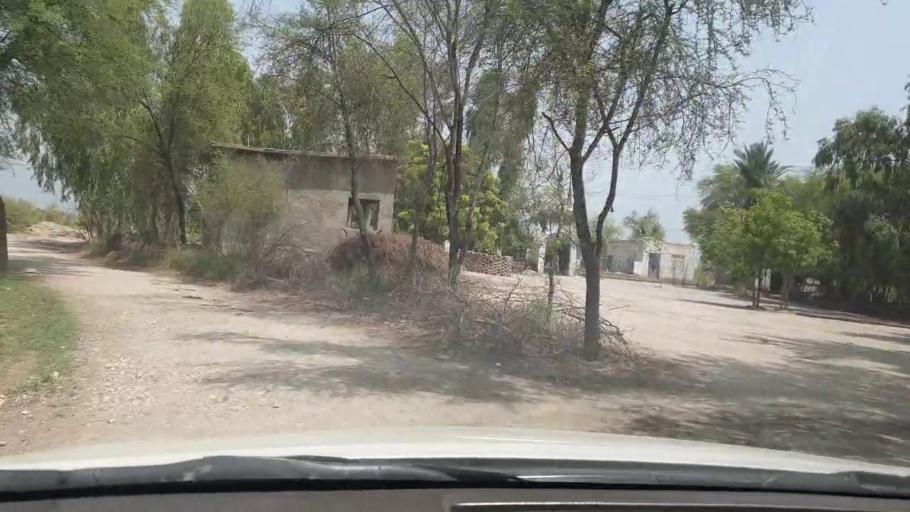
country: PK
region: Sindh
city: Shikarpur
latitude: 28.0264
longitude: 68.6469
